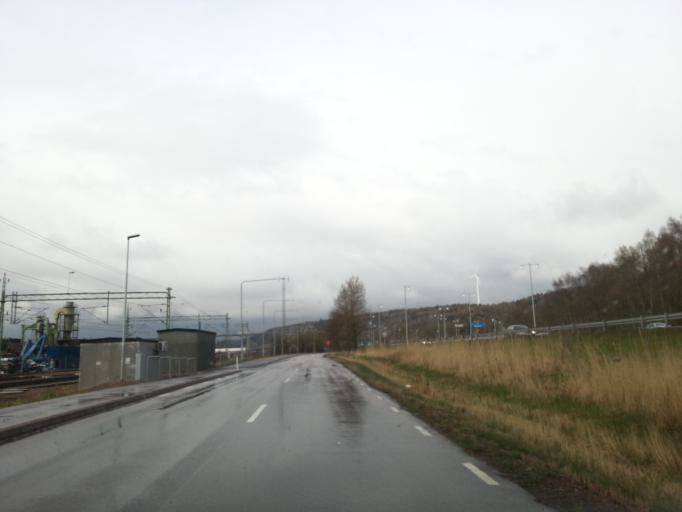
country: SE
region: Vaestra Goetaland
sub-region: Goteborg
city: Hammarkullen
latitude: 57.7845
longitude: 12.0091
